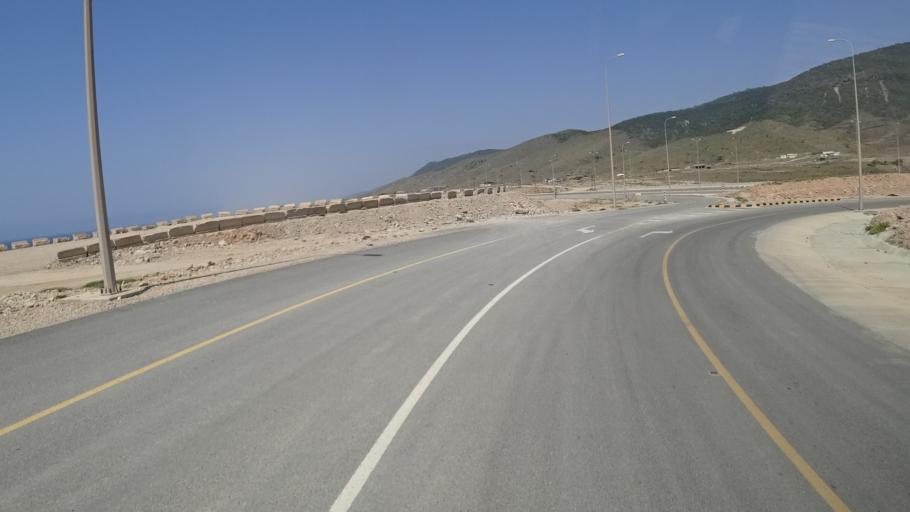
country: OM
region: Zufar
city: Salalah
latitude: 17.0296
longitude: 54.6107
